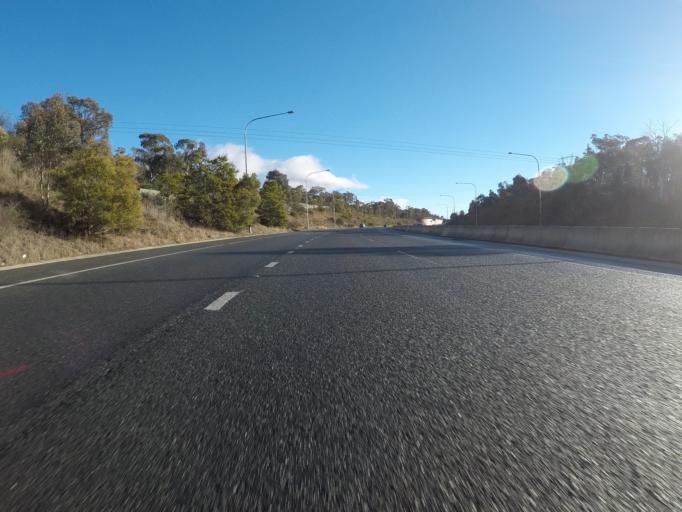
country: AU
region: Australian Capital Territory
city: Macquarie
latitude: -35.2660
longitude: 149.0860
